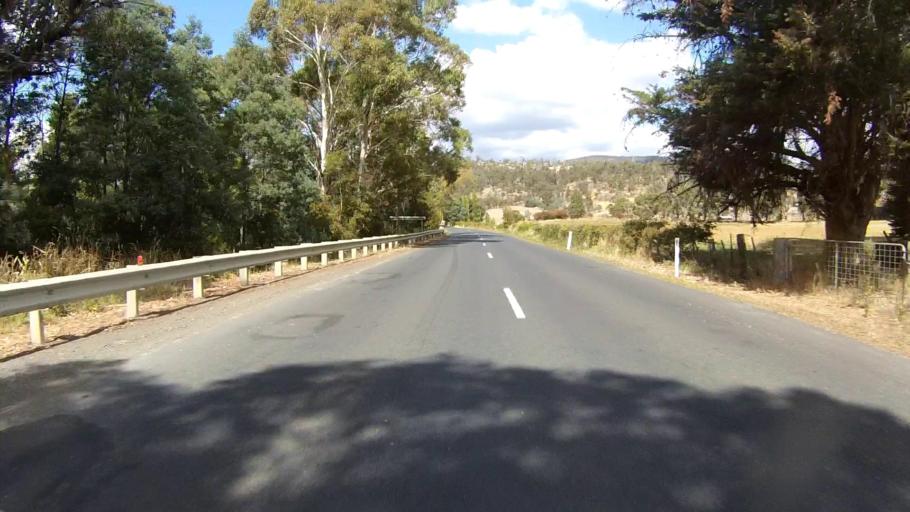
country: AU
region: Tasmania
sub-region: Derwent Valley
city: New Norfolk
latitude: -42.7723
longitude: 147.0273
